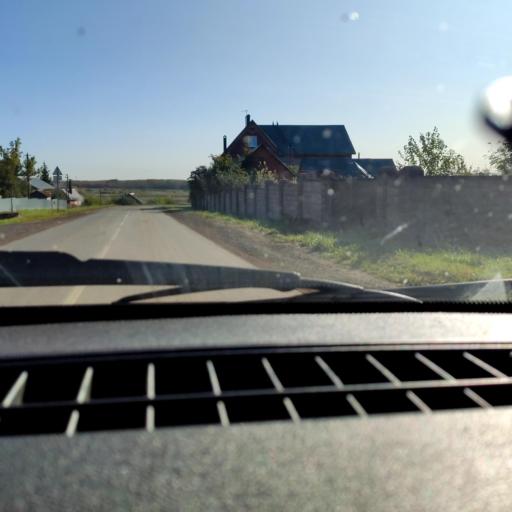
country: RU
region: Bashkortostan
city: Avdon
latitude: 54.6058
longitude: 55.7905
